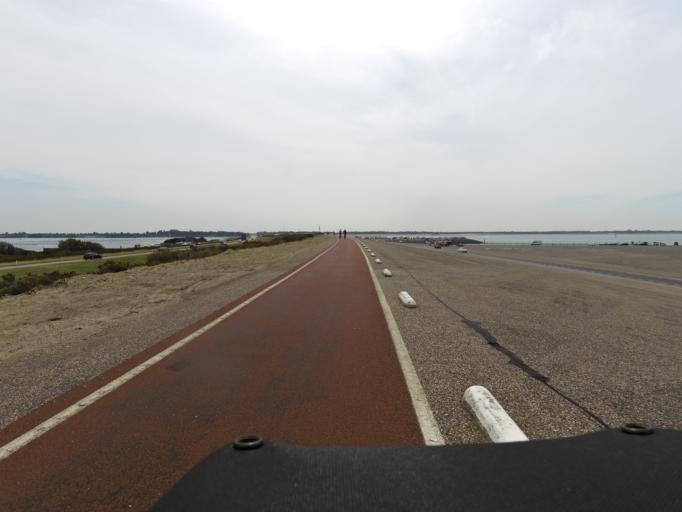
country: NL
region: Zeeland
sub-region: Schouwen-Duiveland
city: Scharendijke
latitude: 51.7507
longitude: 3.8268
